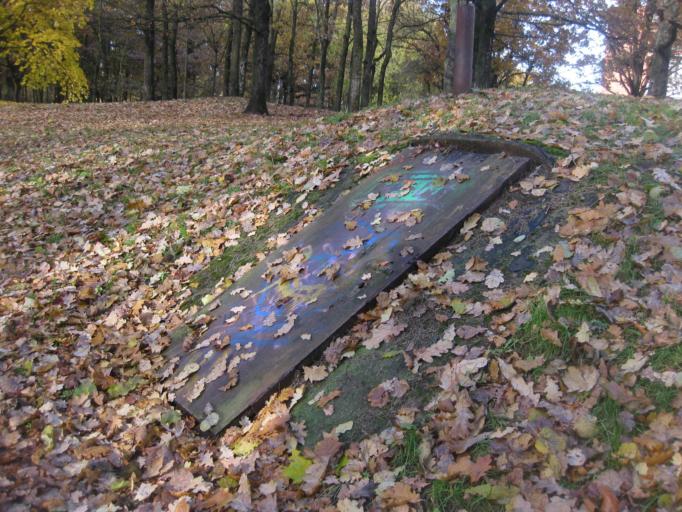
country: LT
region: Kauno apskritis
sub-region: Kaunas
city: Kaunas
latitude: 54.8993
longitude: 23.9301
